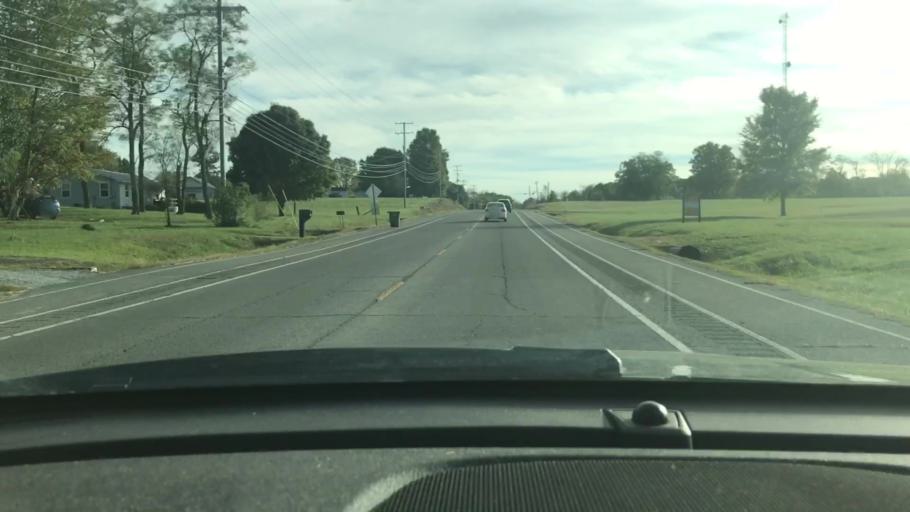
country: US
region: Tennessee
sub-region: Sumner County
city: White House
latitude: 36.4434
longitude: -86.6786
